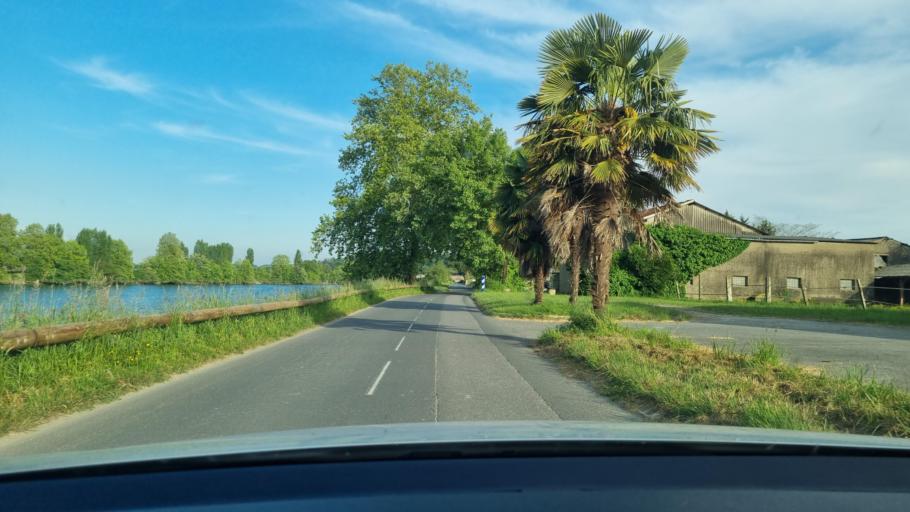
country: FR
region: Aquitaine
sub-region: Departement des Landes
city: Peyrehorade
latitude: 43.5432
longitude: -1.1670
